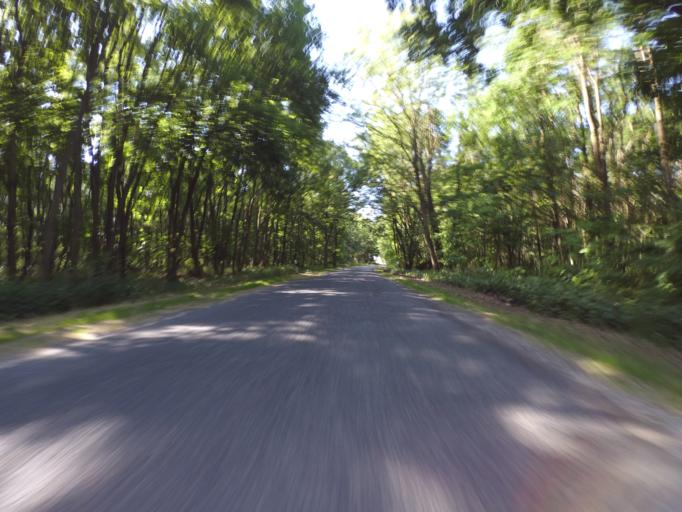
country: DE
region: Brandenburg
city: Triglitz
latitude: 53.2498
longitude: 12.1244
